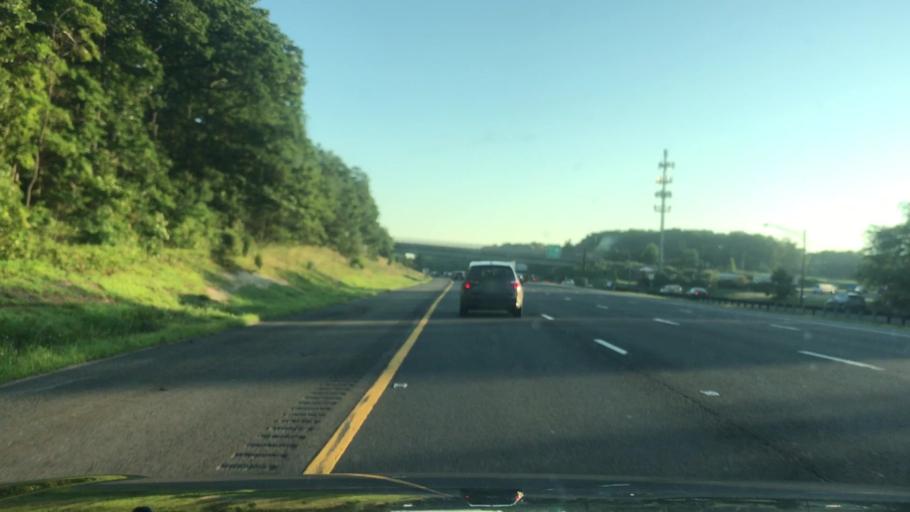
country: US
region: New Jersey
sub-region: Monmouth County
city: Shark River Hills
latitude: 40.1680
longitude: -74.1004
